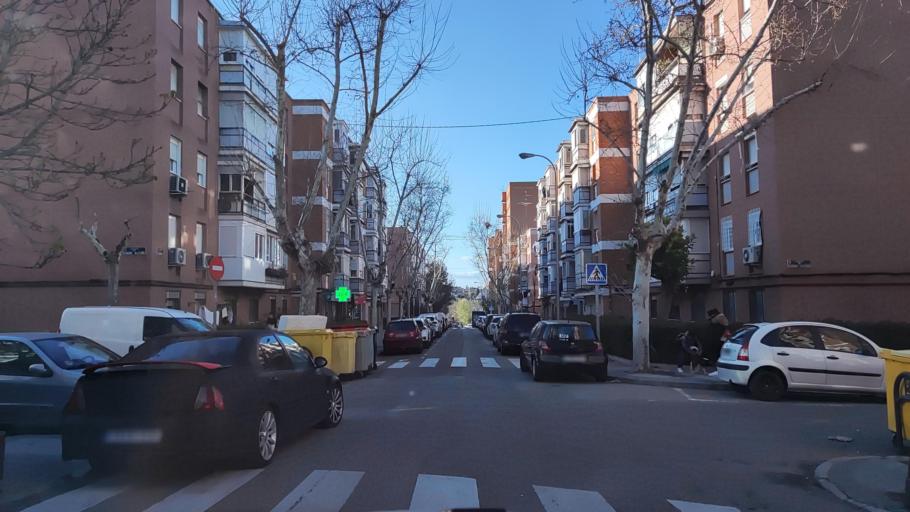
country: ES
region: Madrid
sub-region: Provincia de Madrid
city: Latina
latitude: 40.3980
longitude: -3.7741
